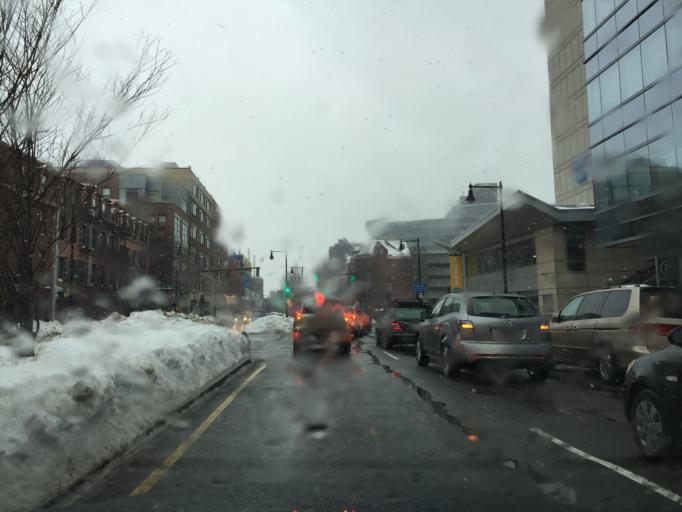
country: US
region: Massachusetts
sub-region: Suffolk County
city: Boston
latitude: 42.3613
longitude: -71.0660
